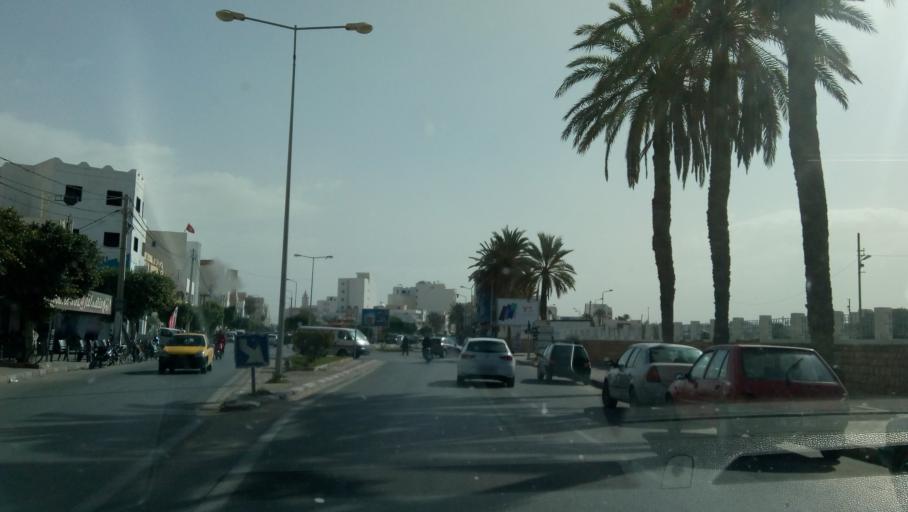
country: TN
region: Qabis
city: Gabes
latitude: 33.8849
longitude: 10.0954
